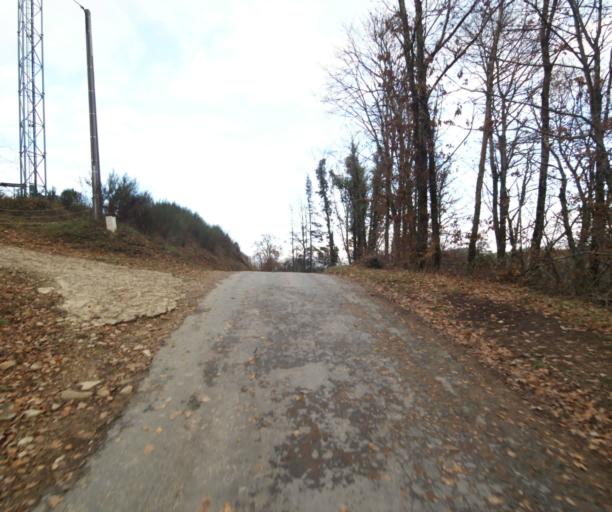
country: FR
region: Limousin
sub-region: Departement de la Correze
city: Laguenne
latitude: 45.2278
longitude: 1.7858
